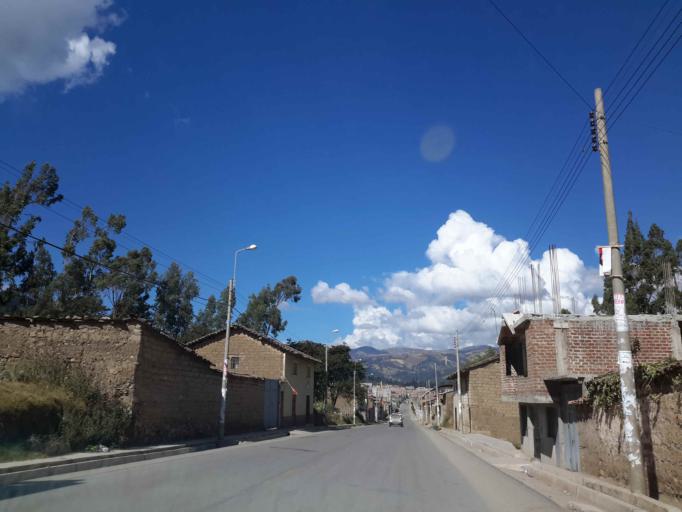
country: PE
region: Apurimac
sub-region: Provincia de Andahuaylas
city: Talavera
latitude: -13.6508
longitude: -73.4396
